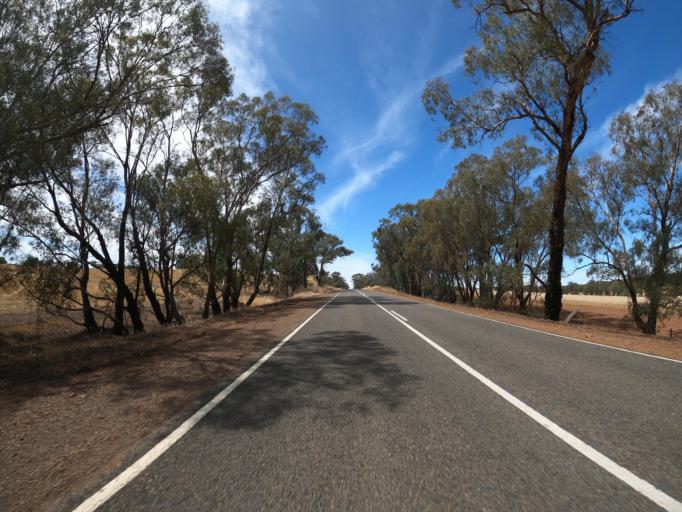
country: AU
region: Victoria
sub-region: Benalla
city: Benalla
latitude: -36.3475
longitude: 145.9613
